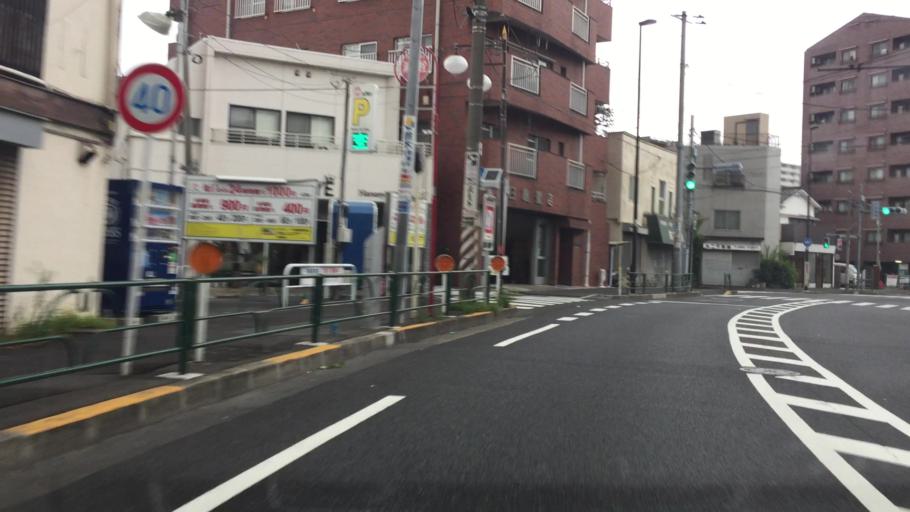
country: JP
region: Saitama
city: Soka
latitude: 35.7460
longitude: 139.7949
